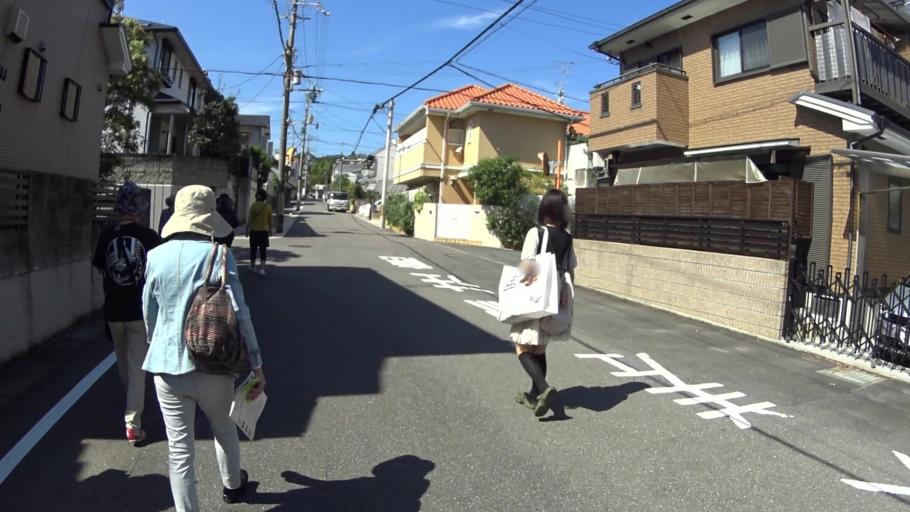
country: JP
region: Kyoto
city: Muko
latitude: 34.9442
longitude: 135.7022
